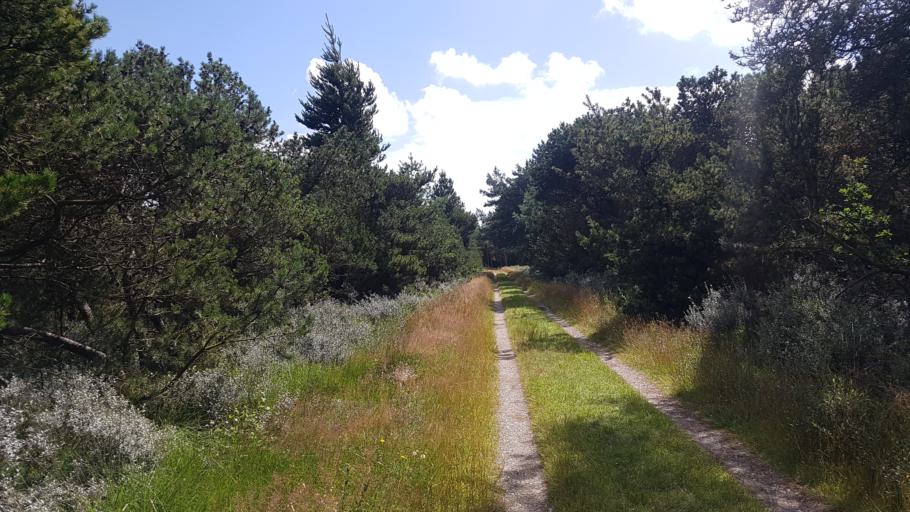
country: DE
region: Schleswig-Holstein
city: List
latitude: 55.1193
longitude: 8.5384
